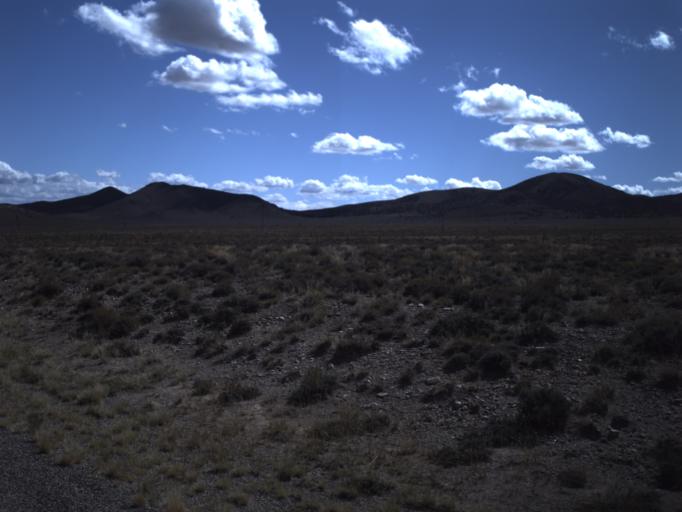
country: US
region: Utah
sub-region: Beaver County
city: Milford
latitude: 38.4300
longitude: -113.1259
